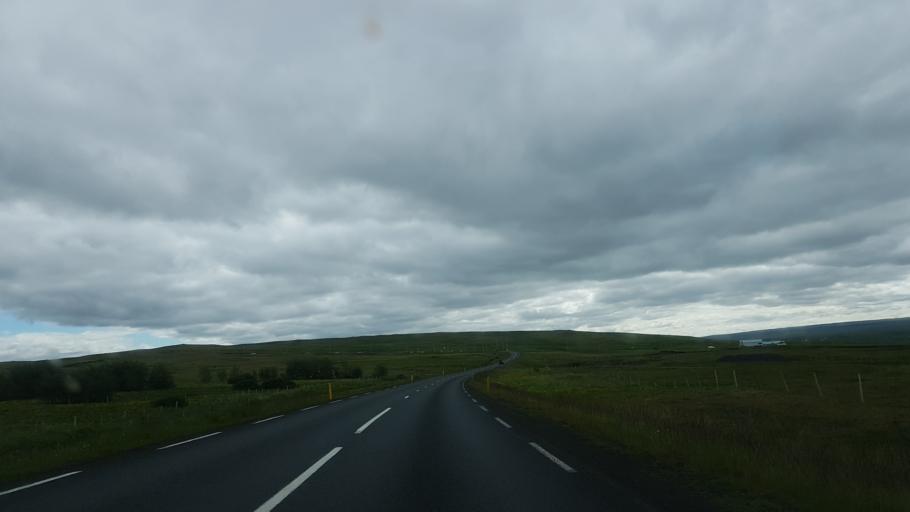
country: IS
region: Northwest
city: Saudarkrokur
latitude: 65.3594
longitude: -20.8904
